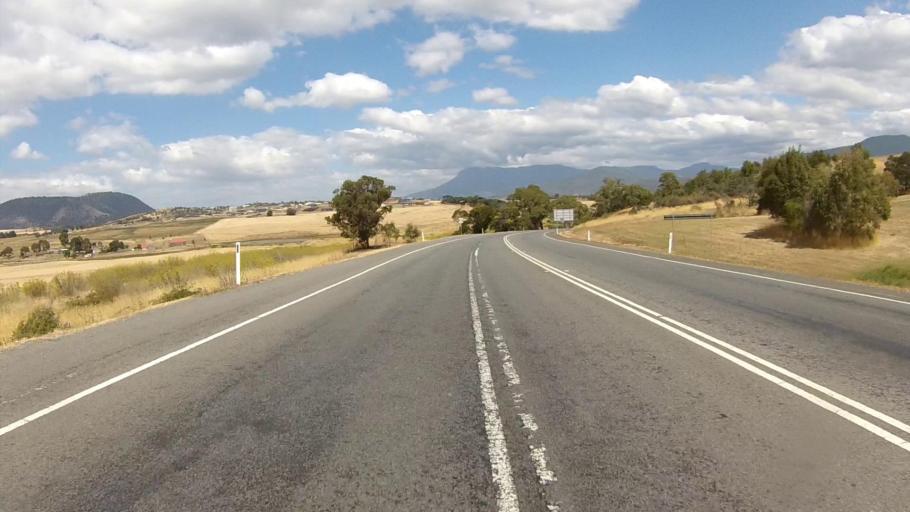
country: AU
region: Tasmania
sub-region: Brighton
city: Old Beach
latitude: -42.7519
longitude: 147.2725
